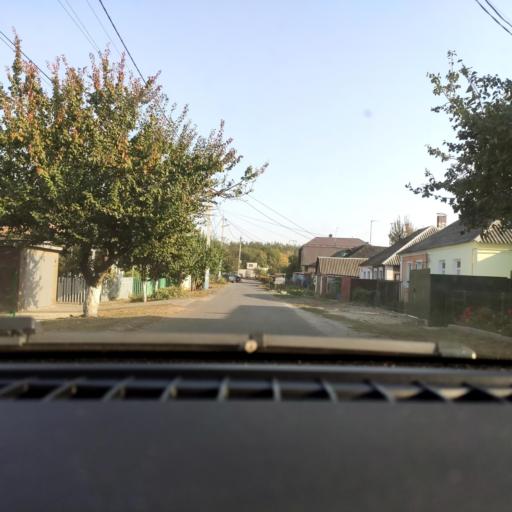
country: RU
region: Voronezj
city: Voronezh
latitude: 51.6736
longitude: 39.2680
